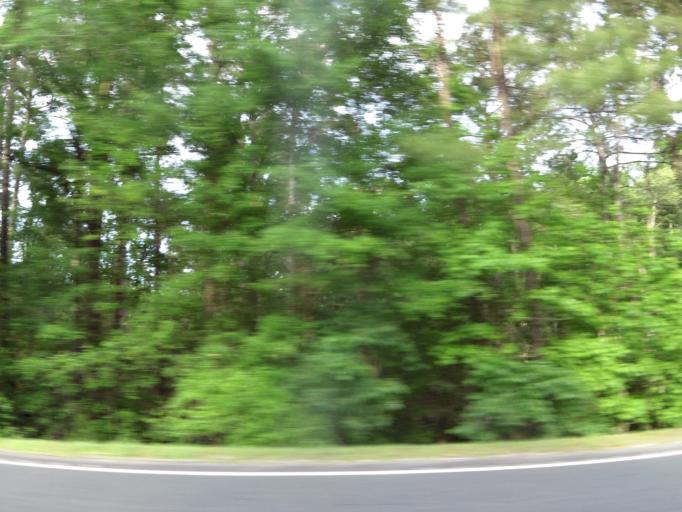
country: US
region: South Carolina
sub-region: Jasper County
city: Hardeeville
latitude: 32.3647
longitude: -81.0948
